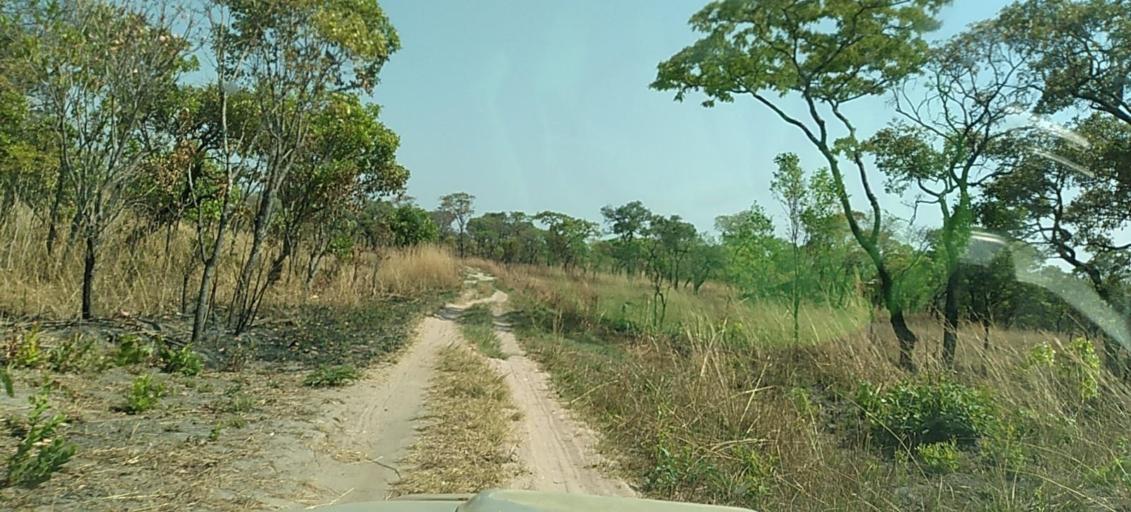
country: ZM
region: North-Western
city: Kalengwa
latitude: -13.3119
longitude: 24.8121
